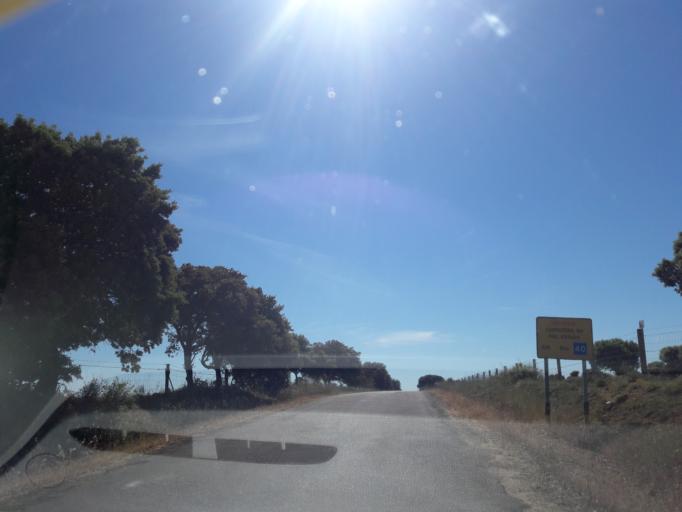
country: ES
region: Castille and Leon
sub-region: Provincia de Salamanca
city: Vega de Tirados
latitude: 41.0506
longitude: -5.8835
